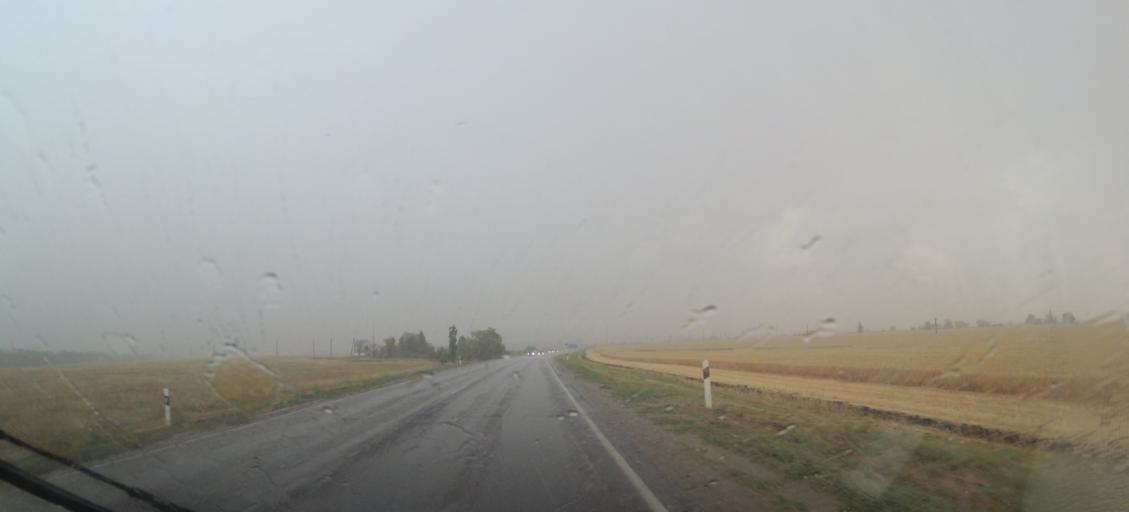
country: RU
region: Rostov
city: Proletarsk
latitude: 46.6750
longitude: 41.6990
